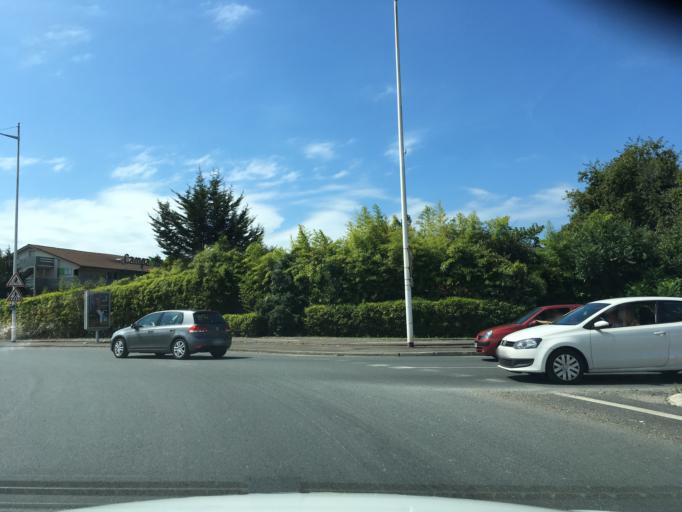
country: FR
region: Aquitaine
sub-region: Departement des Pyrenees-Atlantiques
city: Bayonne
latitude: 43.4915
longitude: -1.4538
